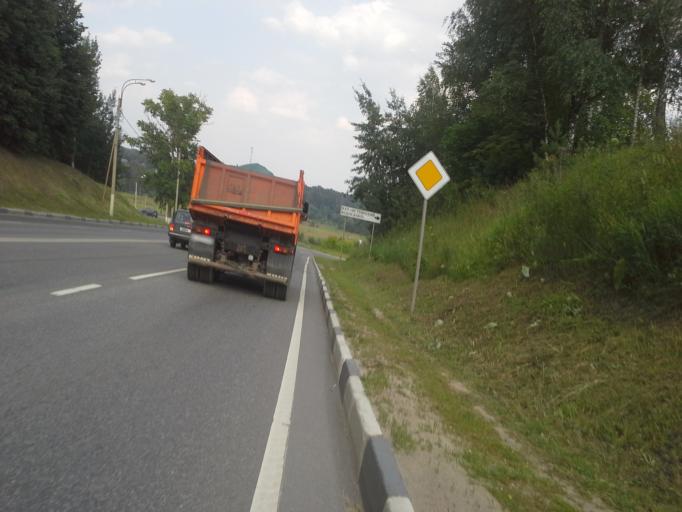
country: RU
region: Moskovskaya
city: Istra
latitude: 55.9153
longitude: 36.8391
